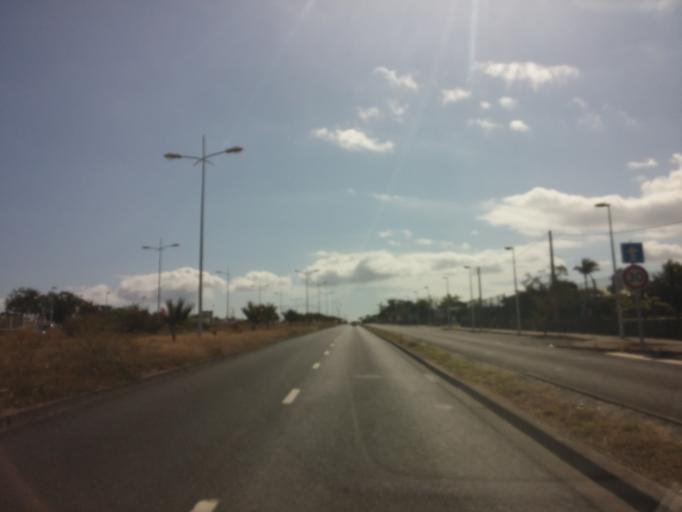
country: RE
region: Reunion
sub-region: Reunion
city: Le Port
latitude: -20.9685
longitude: 55.2956
